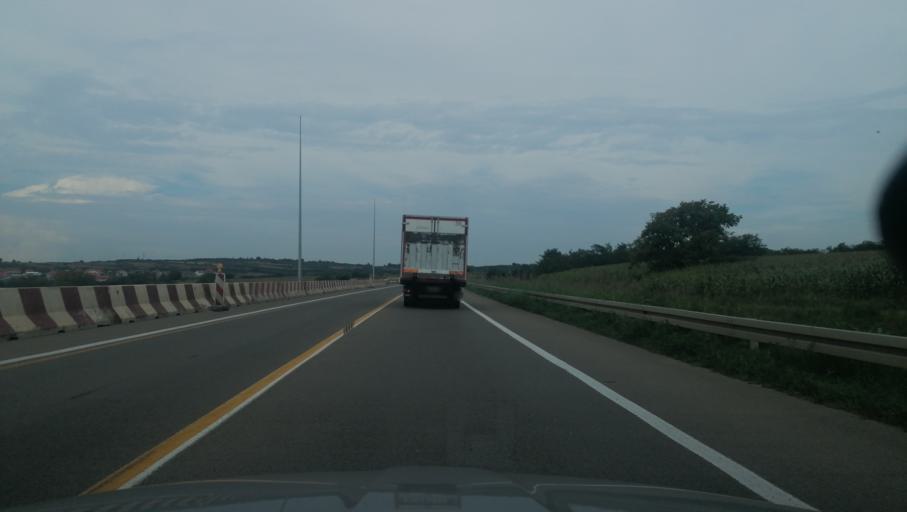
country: RS
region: Central Serbia
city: Sremcica
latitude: 44.7142
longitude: 20.3907
